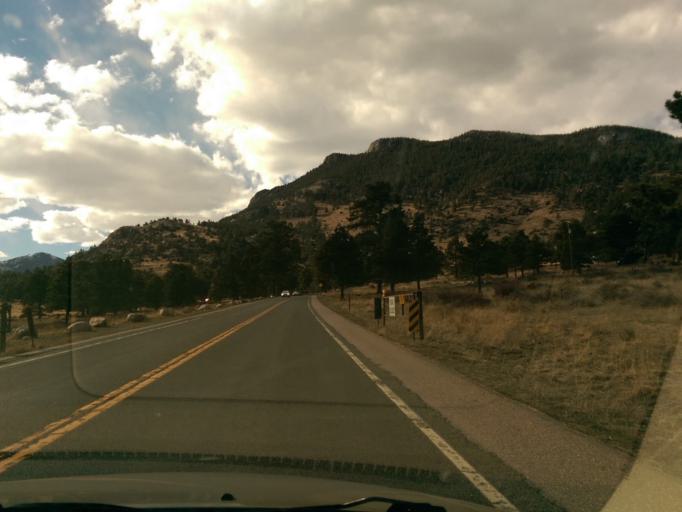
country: US
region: Colorado
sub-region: Larimer County
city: Estes Park
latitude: 40.3681
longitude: -105.5645
